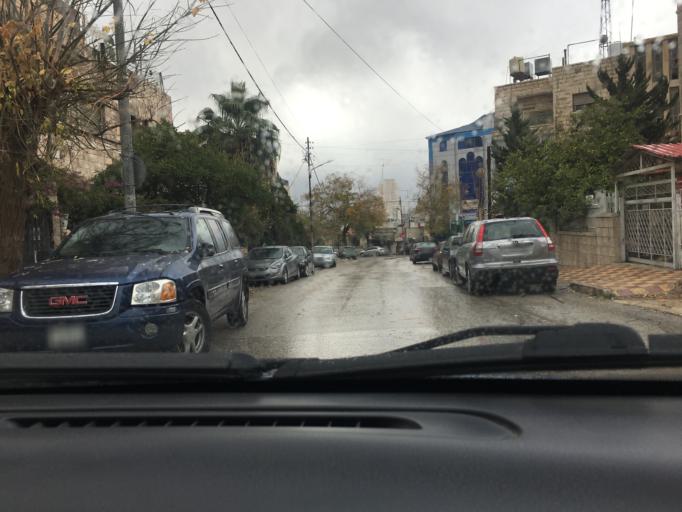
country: JO
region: Amman
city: Amman
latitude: 31.9629
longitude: 35.9174
